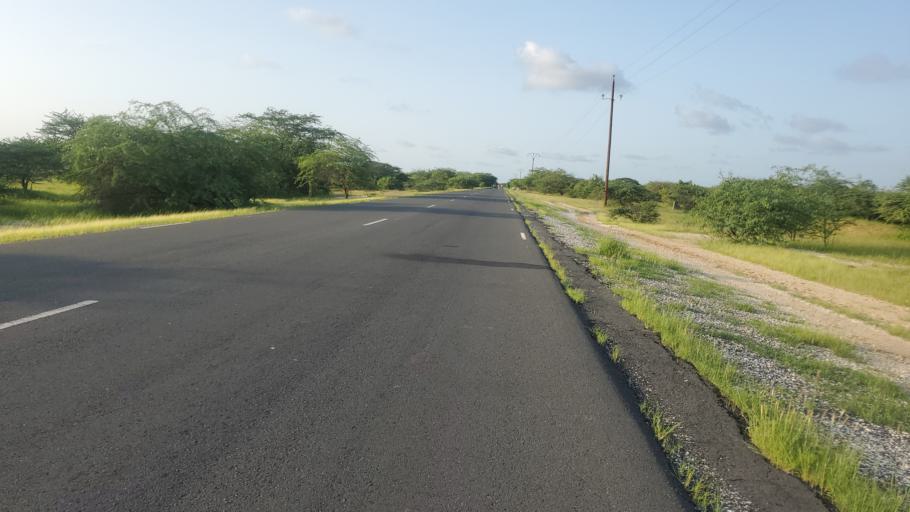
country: SN
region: Saint-Louis
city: Saint-Louis
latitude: 16.1834
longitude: -16.4094
